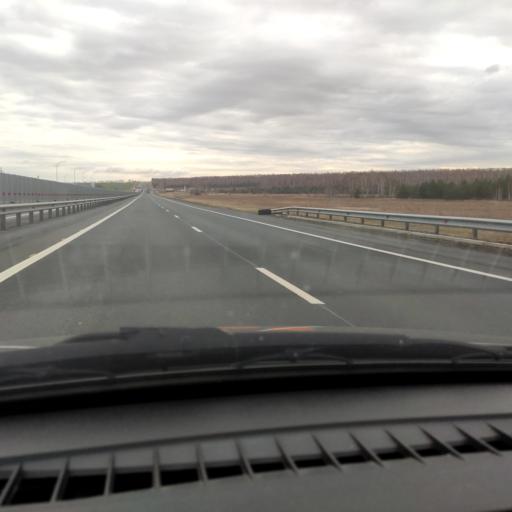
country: RU
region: Samara
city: Mirnyy
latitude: 53.4590
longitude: 50.2139
